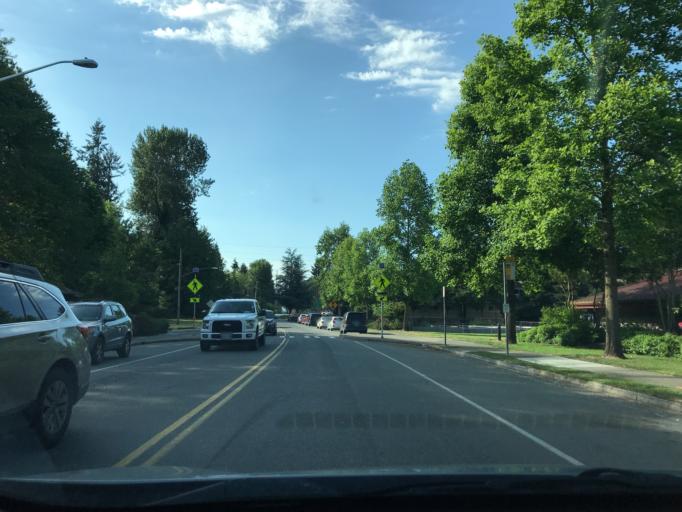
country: US
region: Washington
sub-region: King County
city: Issaquah
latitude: 47.5287
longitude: -122.0397
